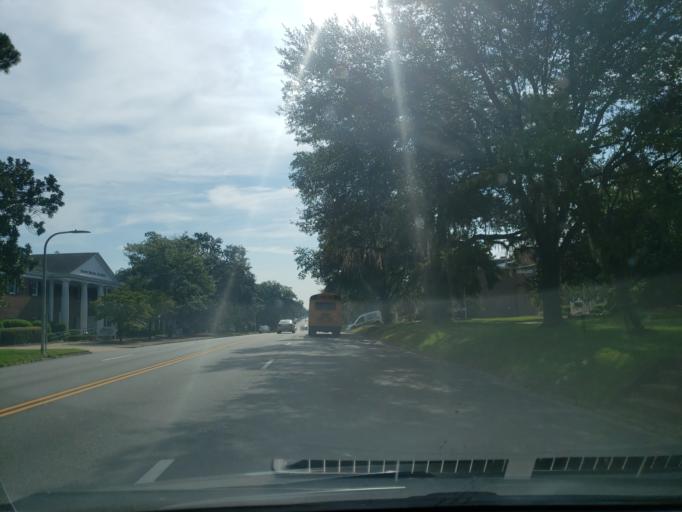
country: US
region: Georgia
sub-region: Dougherty County
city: Albany
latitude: 31.5784
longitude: -84.1614
